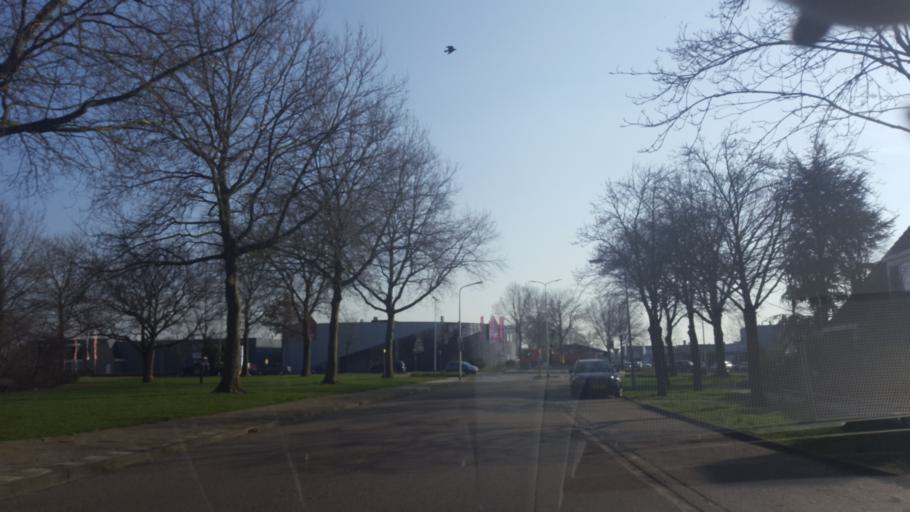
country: NL
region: Limburg
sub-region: Gemeente Weert
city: Weert
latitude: 51.2487
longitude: 5.7373
